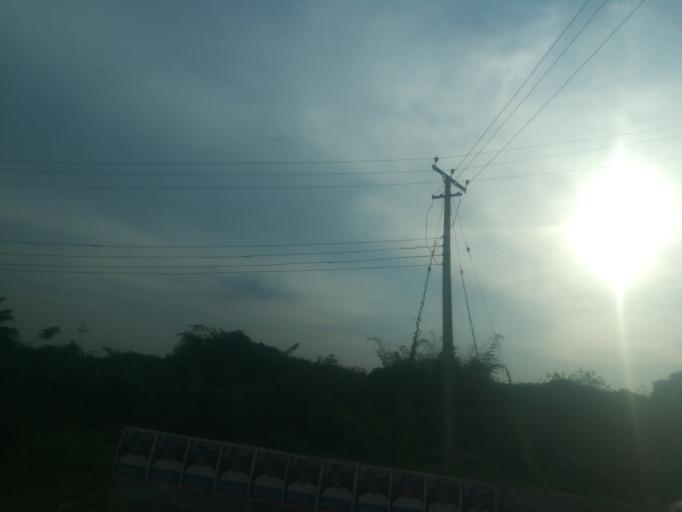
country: NG
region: Ogun
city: Abeokuta
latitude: 7.1588
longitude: 3.3230
